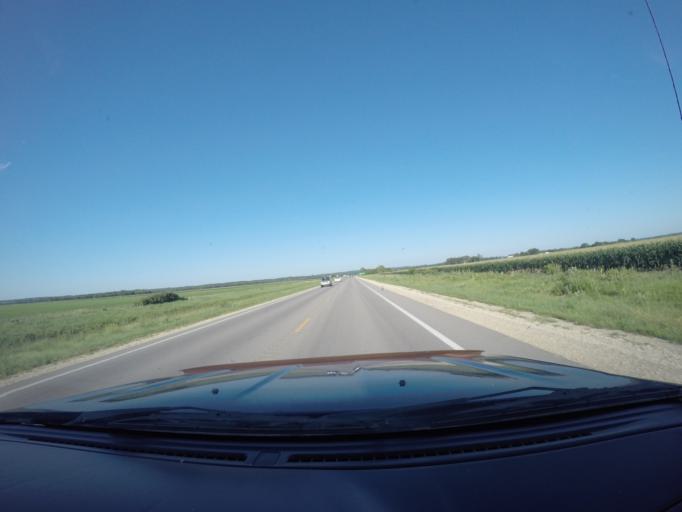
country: US
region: Kansas
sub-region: Jefferson County
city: Oskaloosa
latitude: 39.0873
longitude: -95.4337
